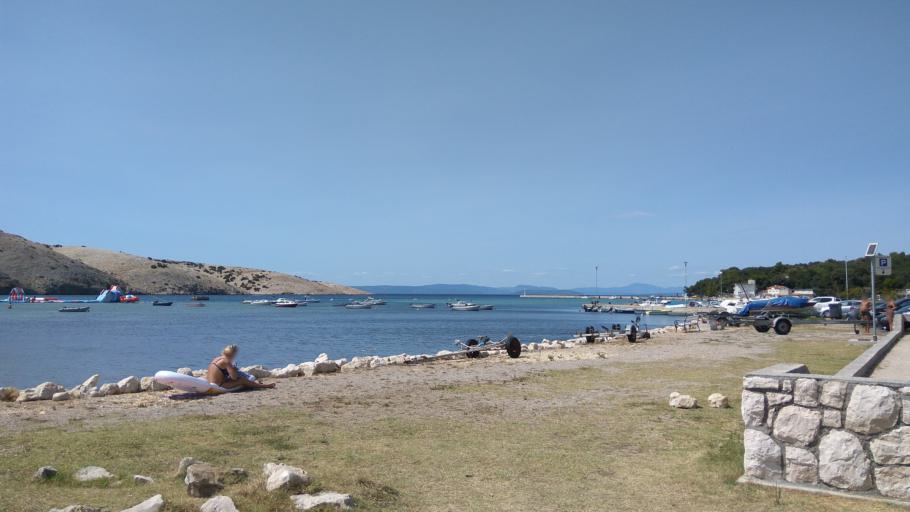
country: HR
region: Primorsko-Goranska
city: Lopar
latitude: 44.8340
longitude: 14.7254
